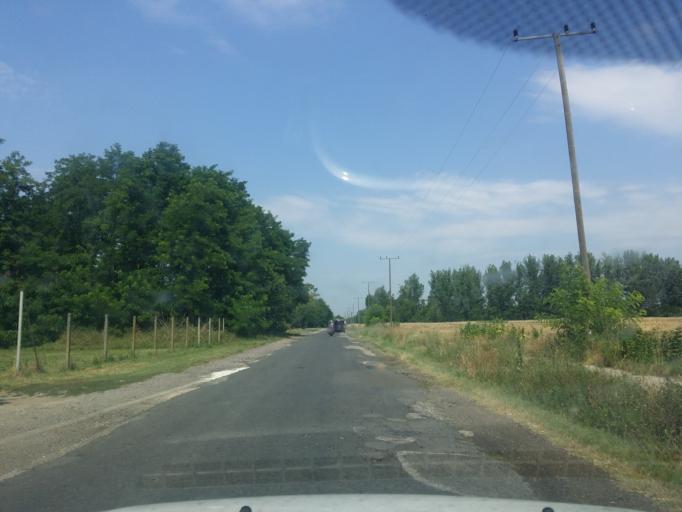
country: HU
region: Bacs-Kiskun
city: Jaszszentlaszlo
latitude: 46.5803
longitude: 19.7335
